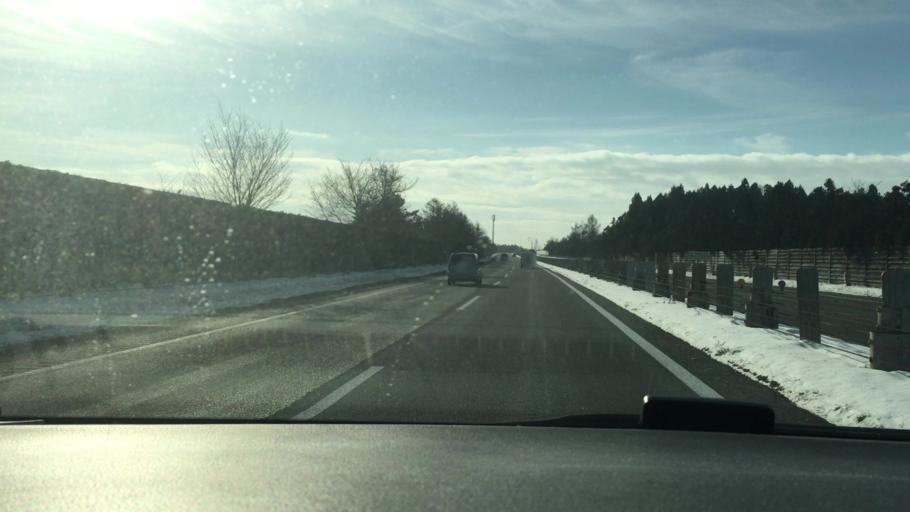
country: JP
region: Iwate
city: Hanamaki
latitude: 39.3498
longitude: 141.0898
